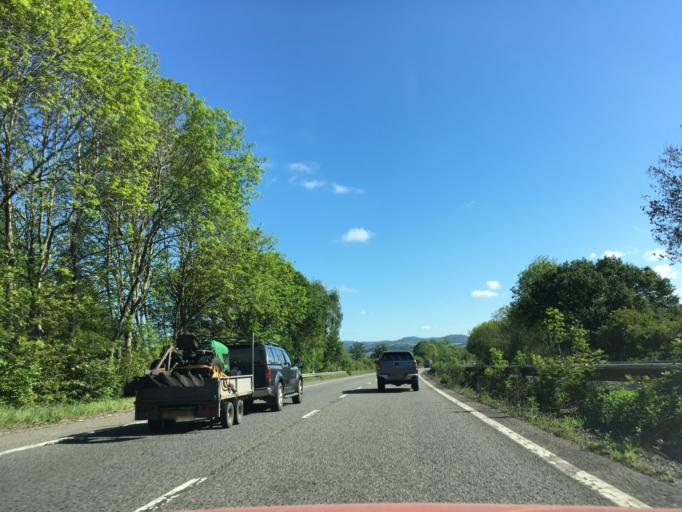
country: GB
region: England
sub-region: Herefordshire
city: Donnington
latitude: 51.9693
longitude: -2.4233
